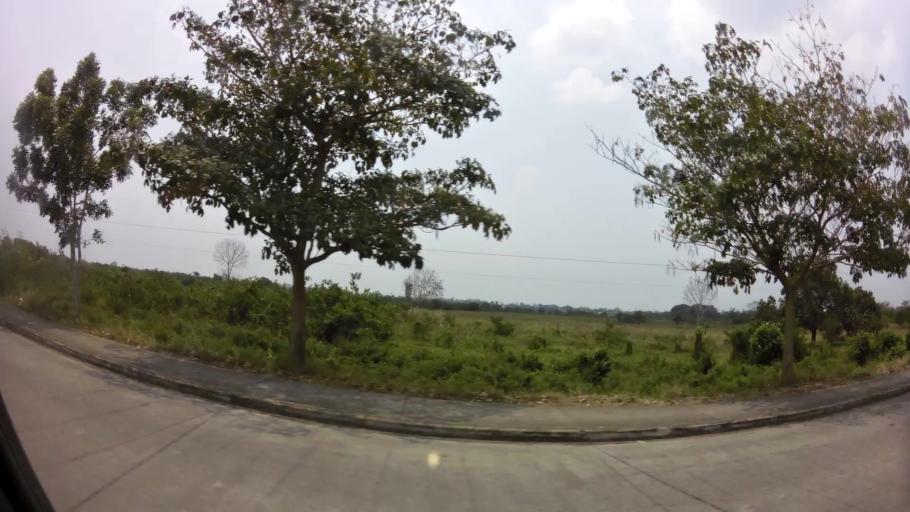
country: HN
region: Cortes
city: La Lima
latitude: 15.4535
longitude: -87.9333
